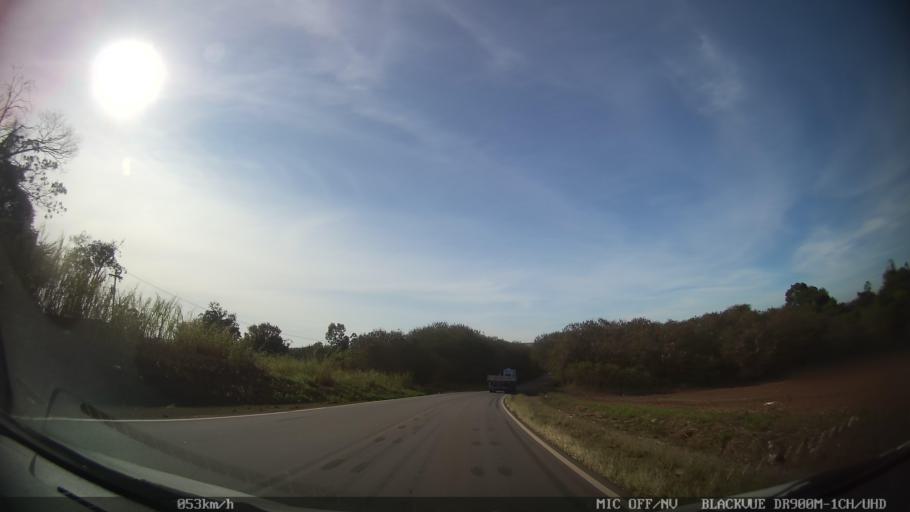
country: BR
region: Sao Paulo
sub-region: Rio Das Pedras
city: Rio das Pedras
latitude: -22.7888
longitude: -47.6332
